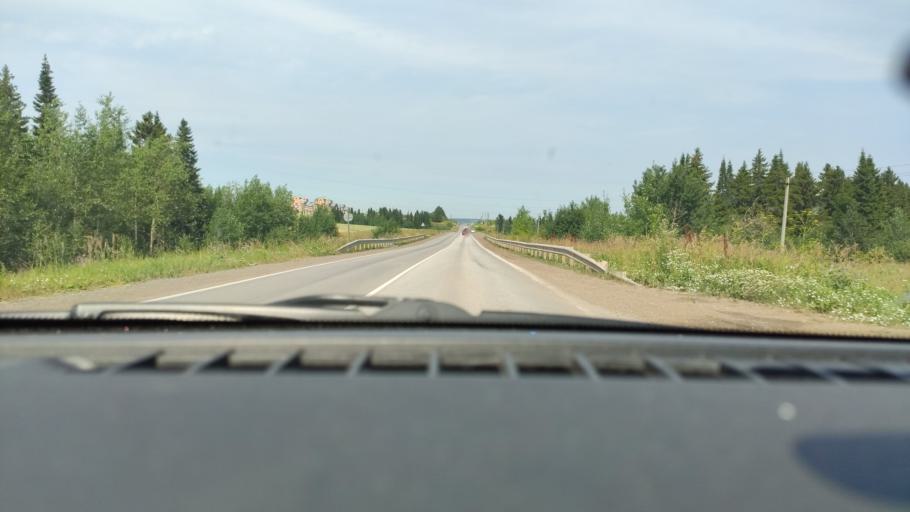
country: RU
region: Perm
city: Lobanovo
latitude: 57.8580
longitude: 56.2960
